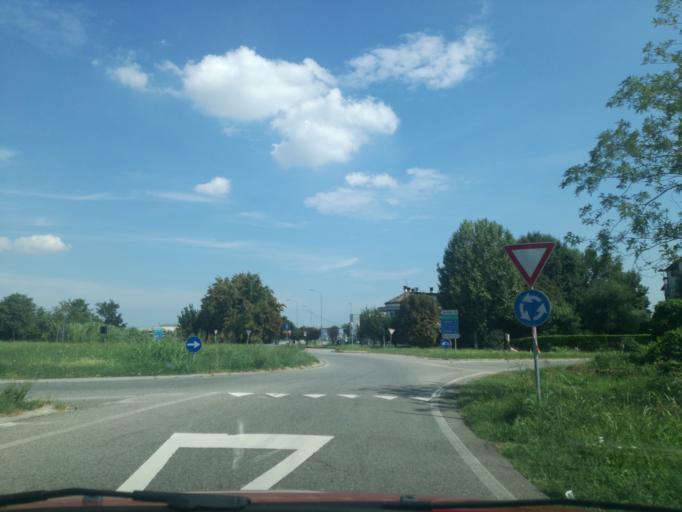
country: IT
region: Lombardy
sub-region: Citta metropolitana di Milano
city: Trezzano Rosa
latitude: 45.5872
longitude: 9.4910
